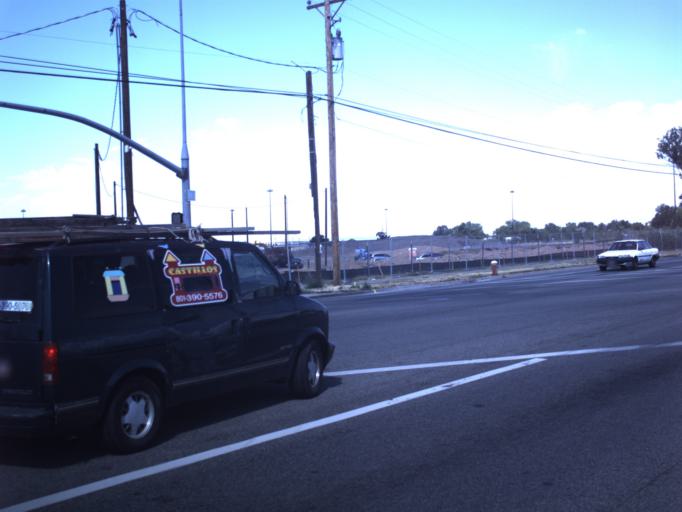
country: US
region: Utah
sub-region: Davis County
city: Clearfield
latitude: 41.0949
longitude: -112.0066
